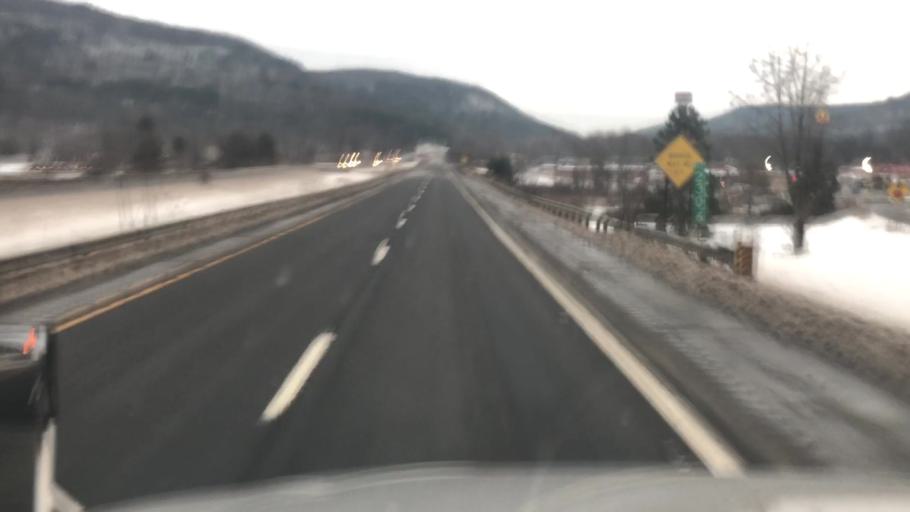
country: US
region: Pennsylvania
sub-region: Susquehanna County
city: Hallstead
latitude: 41.9687
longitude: -75.7395
